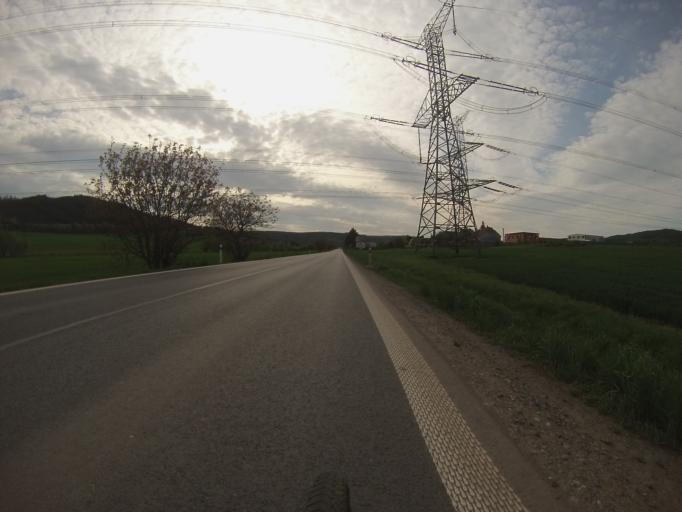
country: CZ
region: South Moravian
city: Drasov
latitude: 49.3249
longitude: 16.4541
